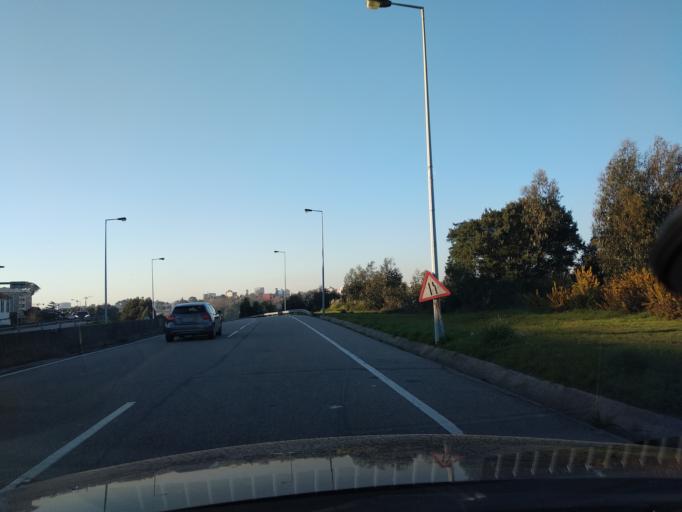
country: PT
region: Porto
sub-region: Vila Nova de Gaia
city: Vila Nova de Gaia
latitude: 41.1421
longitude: -8.6351
